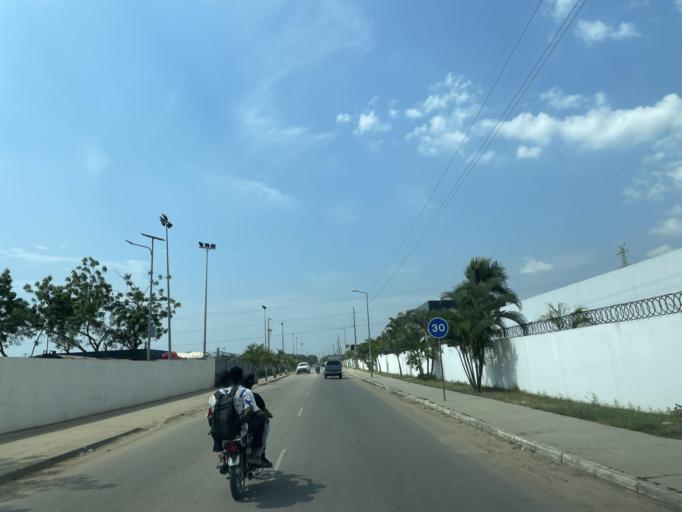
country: AO
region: Luanda
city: Luanda
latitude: -8.9764
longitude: 13.3393
